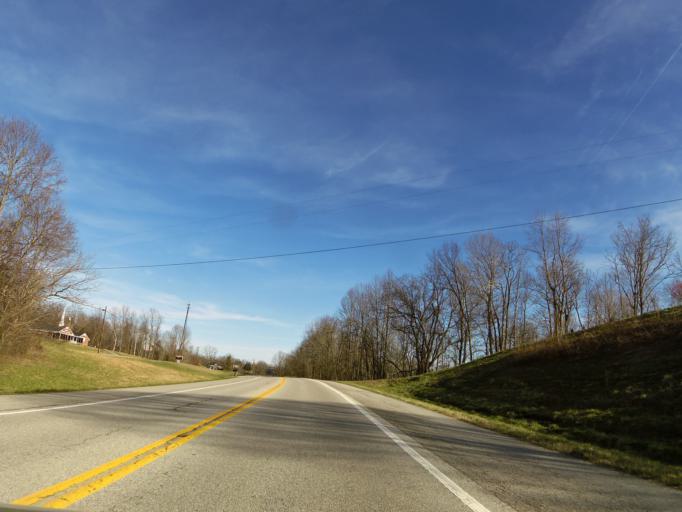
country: US
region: Tennessee
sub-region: Cannon County
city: Woodbury
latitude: 35.8030
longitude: -86.0078
